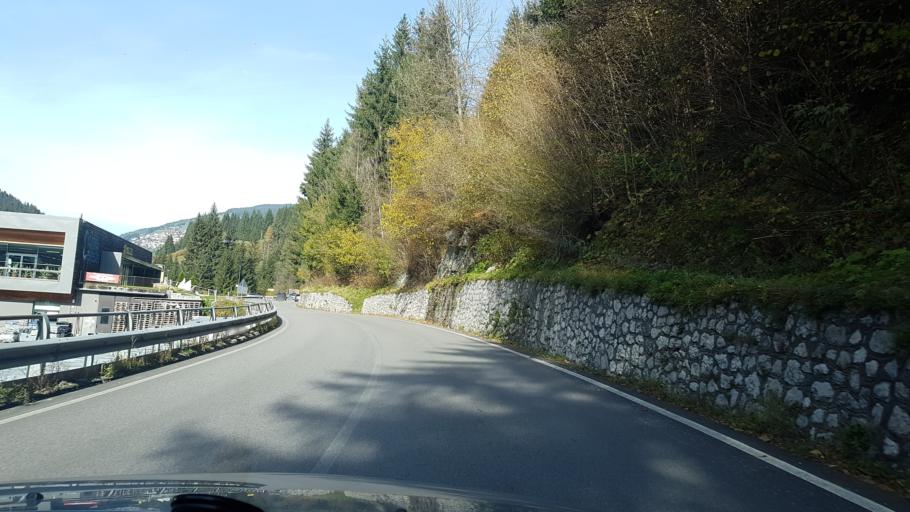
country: IT
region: Veneto
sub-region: Provincia di Belluno
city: Santo Stefano di Cadore
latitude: 46.5635
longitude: 12.5453
